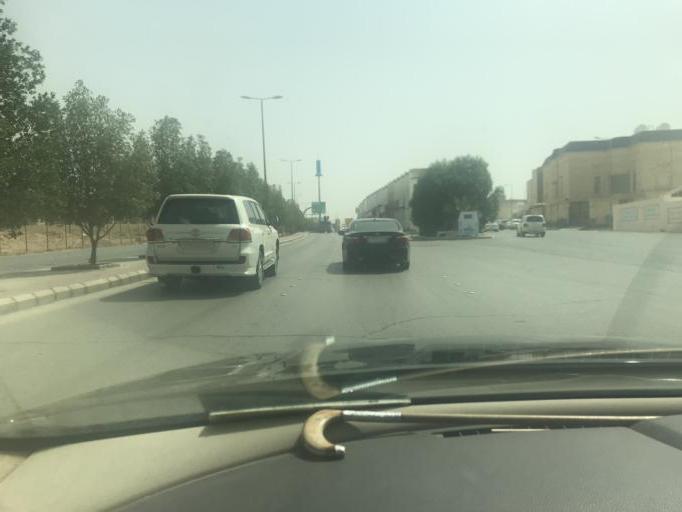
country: SA
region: Ar Riyad
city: Riyadh
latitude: 24.7399
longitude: 46.7844
